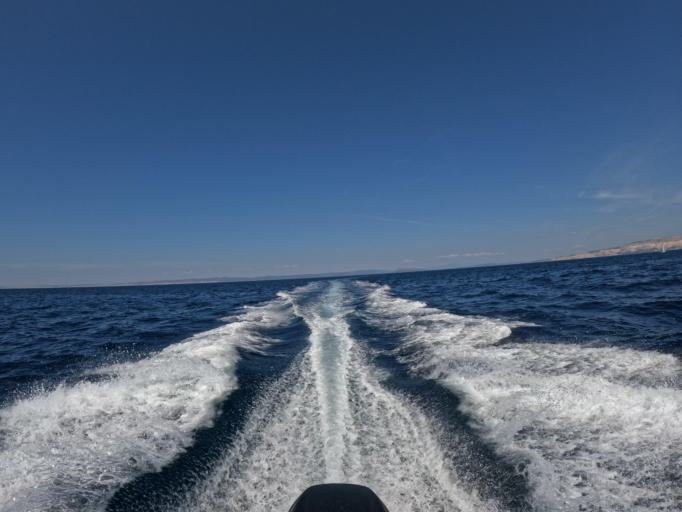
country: HR
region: Primorsko-Goranska
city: Lopar
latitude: 44.8570
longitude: 14.6978
